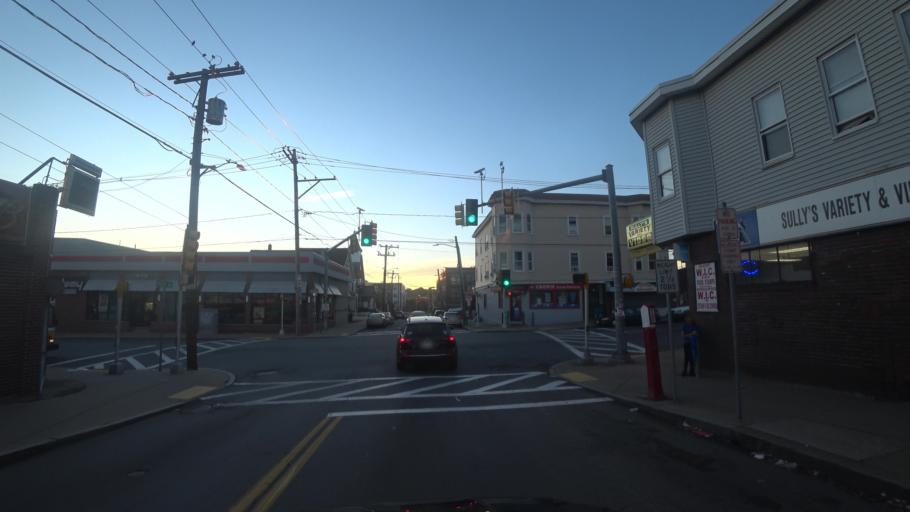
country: US
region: Massachusetts
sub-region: Suffolk County
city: Chelsea
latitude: 42.3998
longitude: -71.0226
